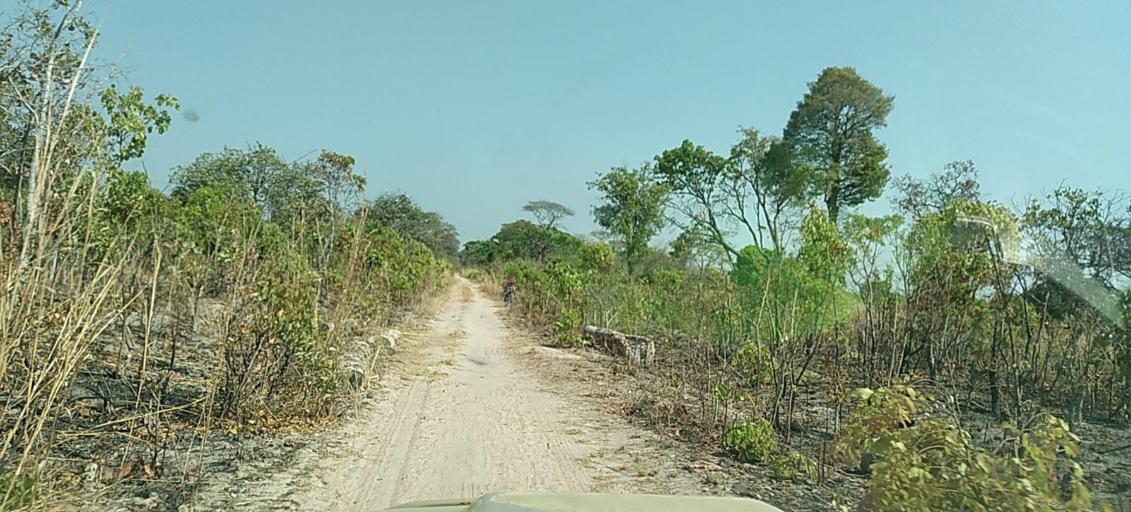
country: ZM
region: North-Western
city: Kalengwa
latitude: -13.3172
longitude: 24.8174
